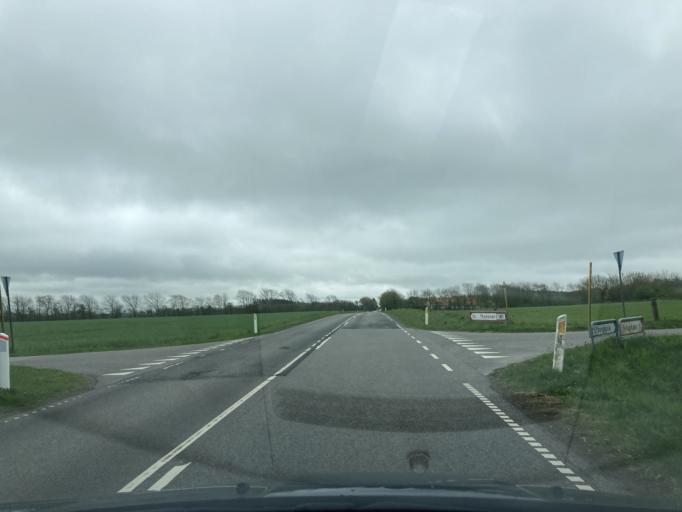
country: DK
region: North Denmark
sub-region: Thisted Kommune
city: Hurup
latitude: 56.8515
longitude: 8.3677
